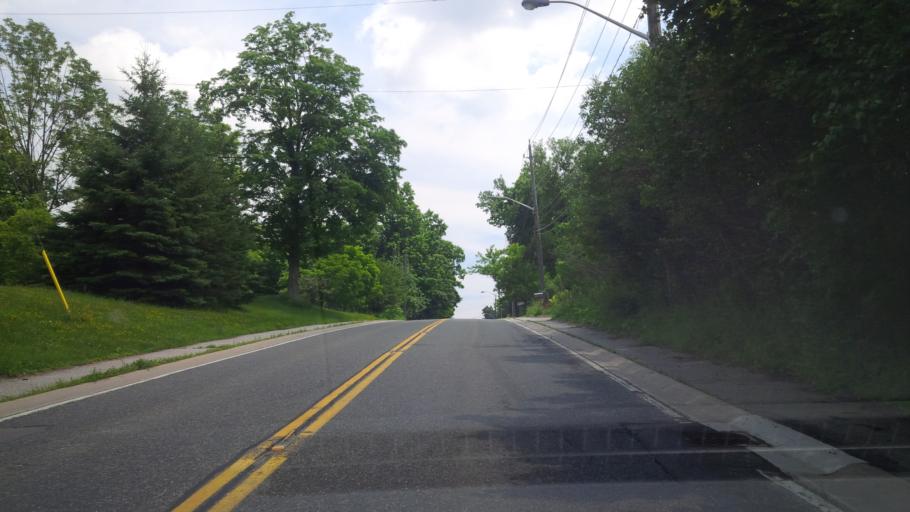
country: CA
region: Ontario
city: Burlington
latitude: 43.4311
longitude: -79.9034
